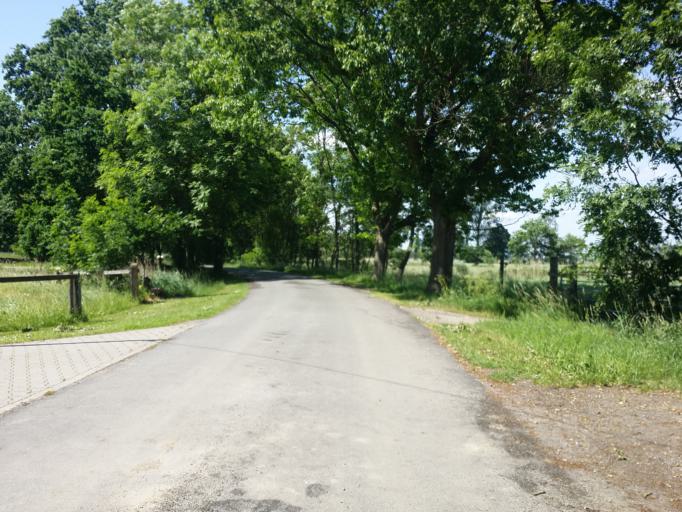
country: DE
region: Lower Saxony
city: Neuenkirchen
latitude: 53.1639
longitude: 8.5129
